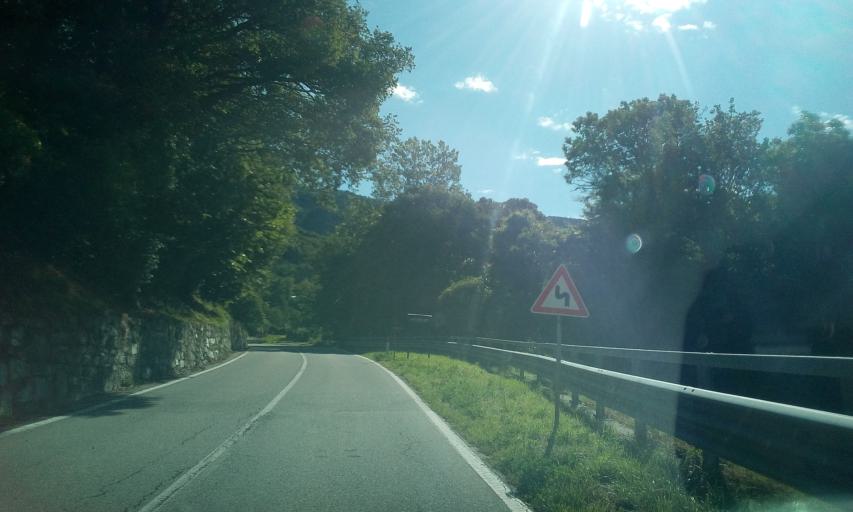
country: IT
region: Aosta Valley
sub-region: Valle d'Aosta
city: Saint-Vincent
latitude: 45.7515
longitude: 7.6591
